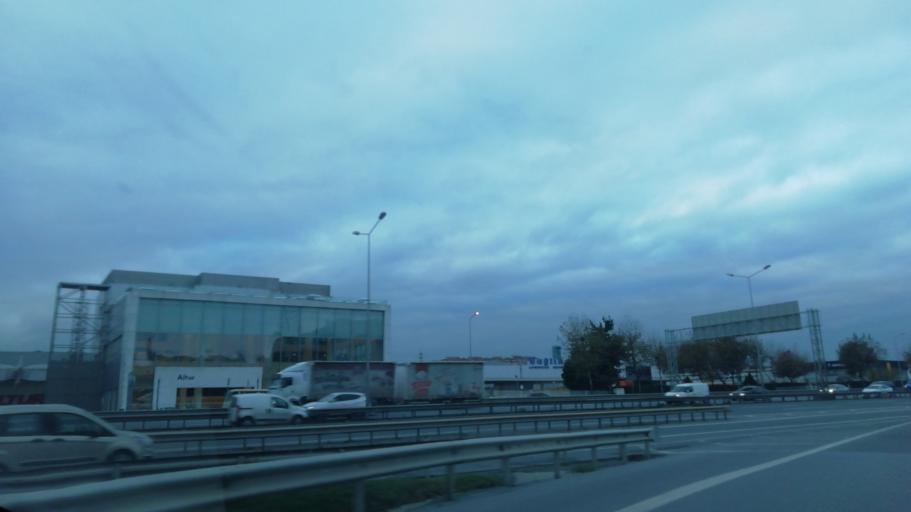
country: TR
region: Istanbul
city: Mahmutbey
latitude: 41.0114
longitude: 28.8129
